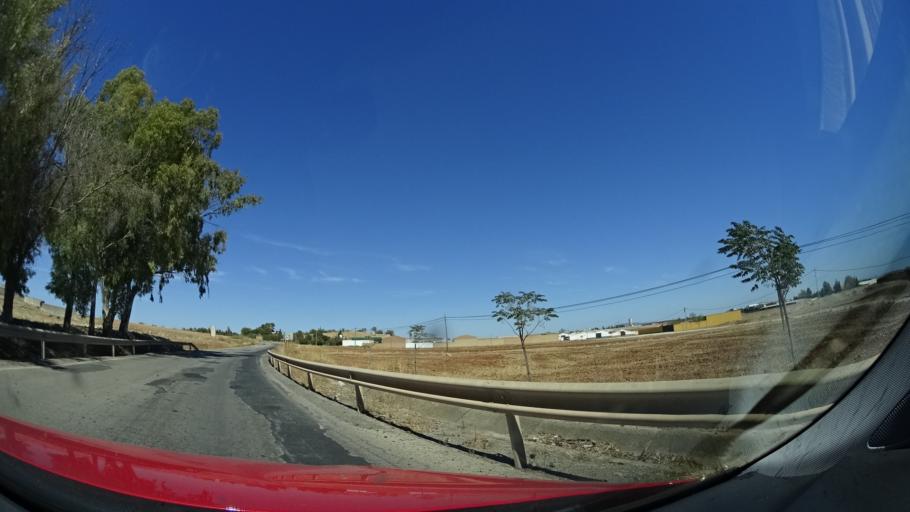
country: ES
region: Andalusia
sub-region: Provincia de Malaga
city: Campillos
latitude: 37.0546
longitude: -4.8641
